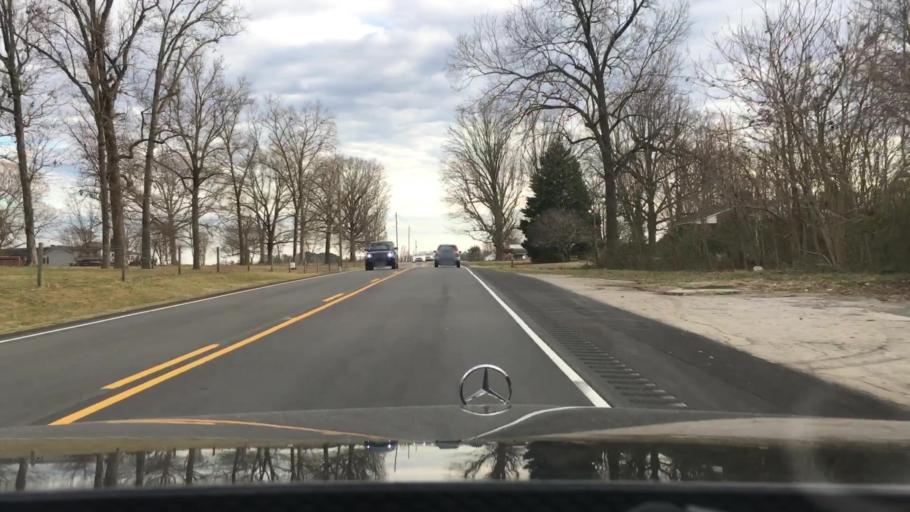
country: US
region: North Carolina
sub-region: Caswell County
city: Yanceyville
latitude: 36.3751
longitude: -79.2607
